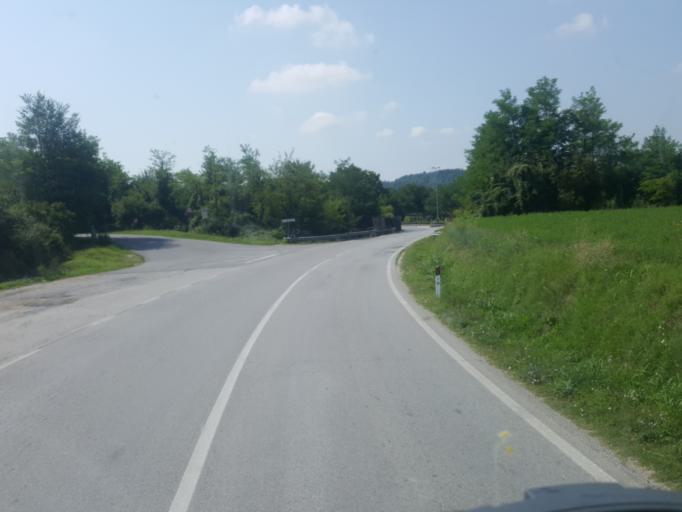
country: IT
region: Piedmont
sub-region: Provincia di Cuneo
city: Narzole
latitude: 44.5987
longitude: 7.8922
